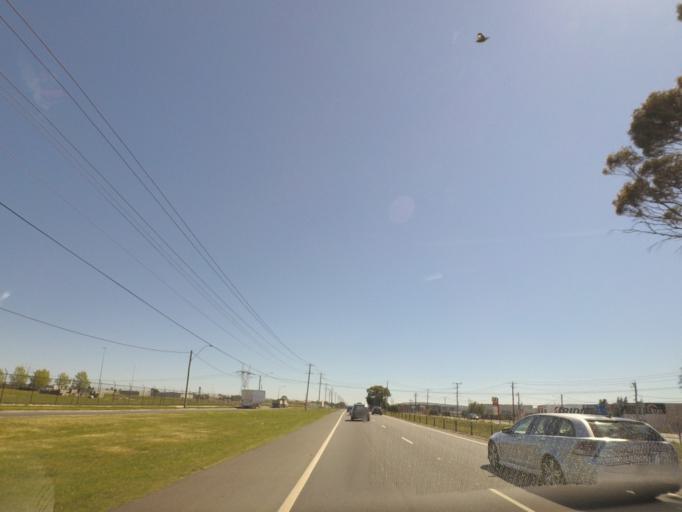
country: AU
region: Victoria
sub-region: Hume
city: Roxburgh Park
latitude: -37.6331
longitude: 144.9495
